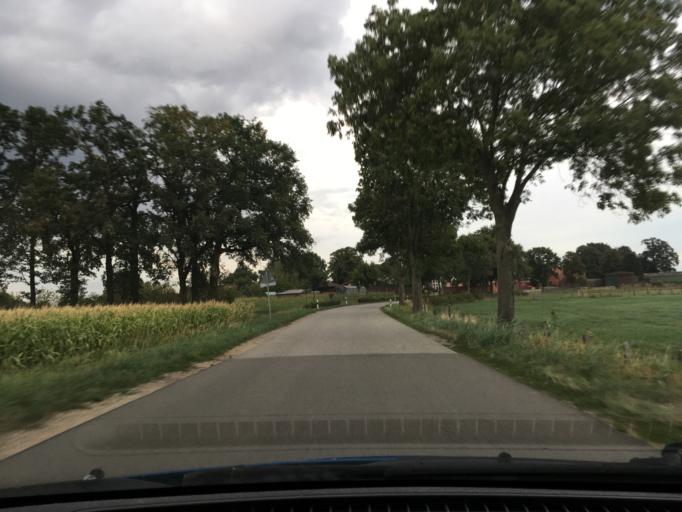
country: DE
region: Schleswig-Holstein
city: Lanze
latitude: 53.3834
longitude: 10.6001
